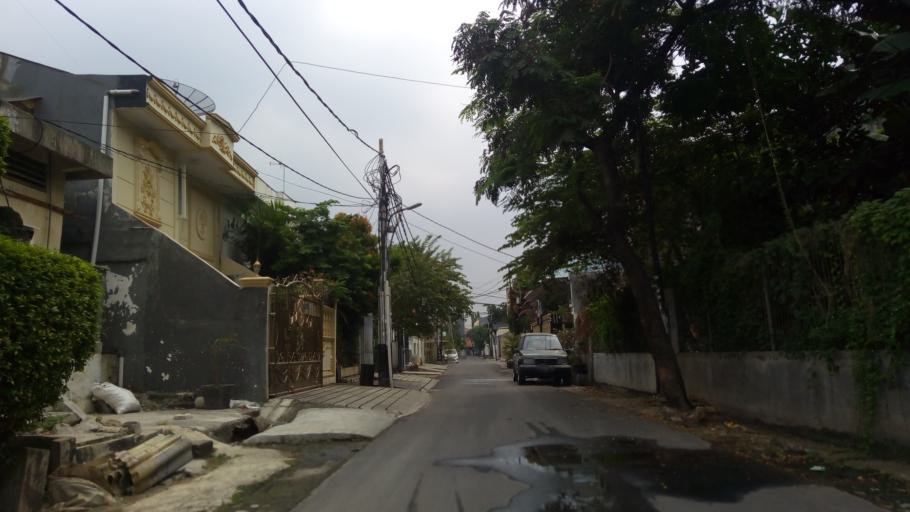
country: ID
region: Jakarta Raya
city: Jakarta
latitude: -6.1566
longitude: 106.8390
